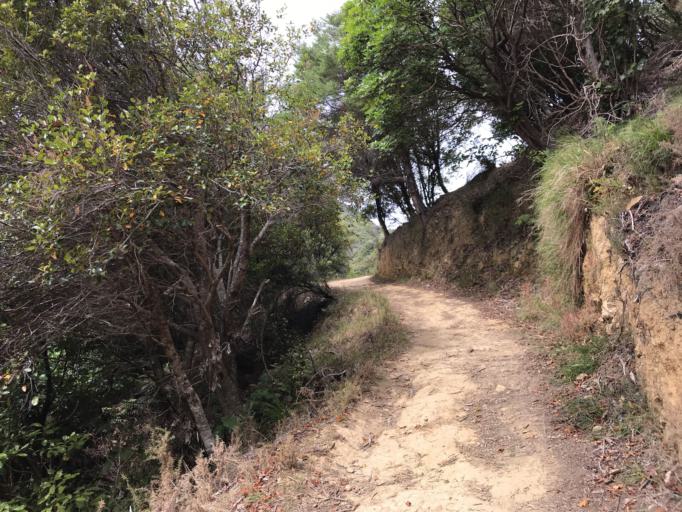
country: NZ
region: Marlborough
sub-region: Marlborough District
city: Picton
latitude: -41.1176
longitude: 174.2027
